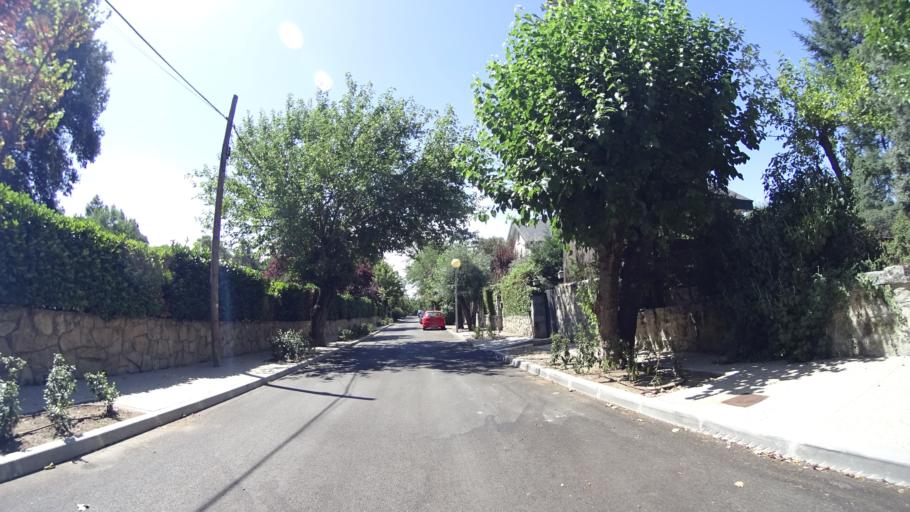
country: ES
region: Madrid
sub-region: Provincia de Madrid
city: Torrelodones
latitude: 40.5733
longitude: -3.9453
